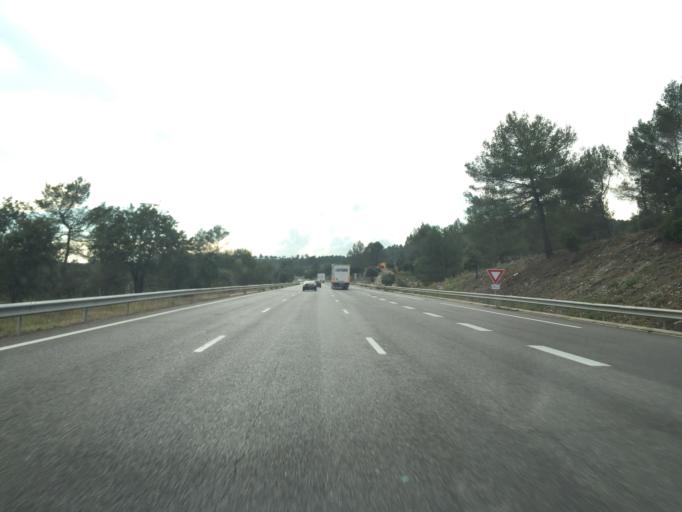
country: FR
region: Provence-Alpes-Cote d'Azur
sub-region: Departement du Var
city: Bras
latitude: 43.4238
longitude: 5.9859
